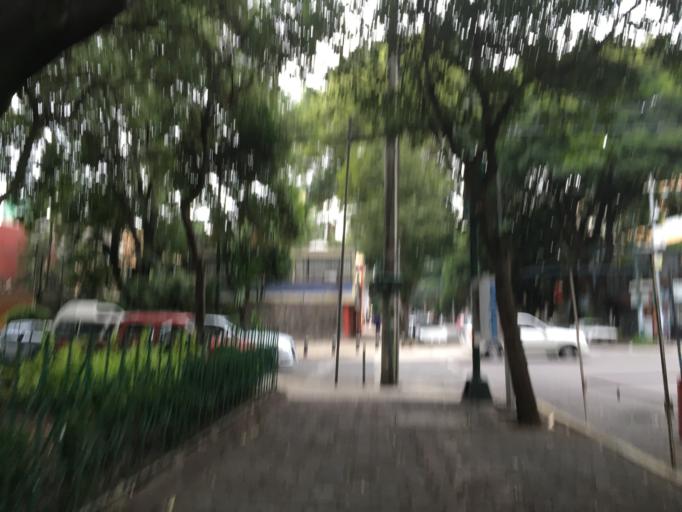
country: MX
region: Mexico City
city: Colonia del Valle
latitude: 19.3792
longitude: -99.1723
